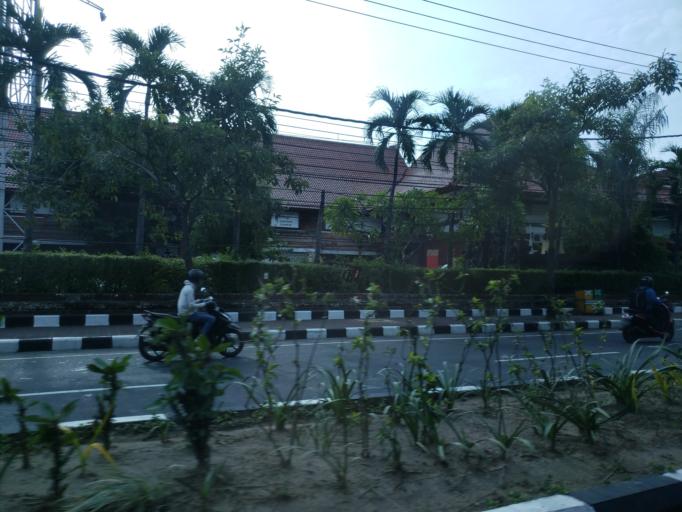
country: ID
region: Bali
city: Jabajero
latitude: -8.7350
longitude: 115.1792
